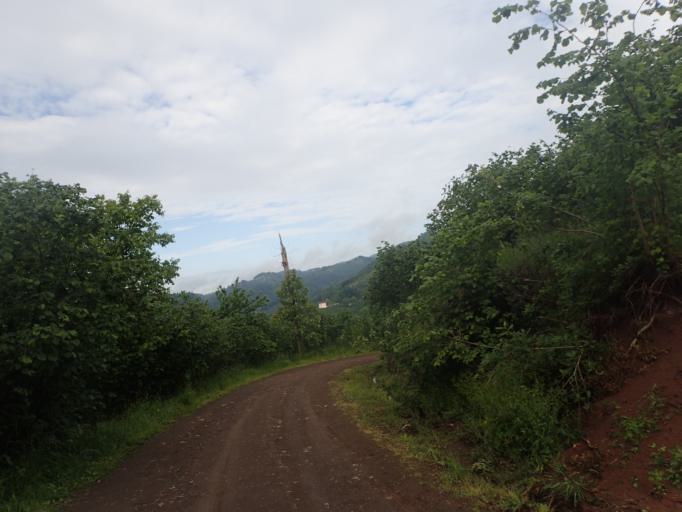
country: TR
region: Samsun
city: Salipazari
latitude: 40.9215
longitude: 36.8635
